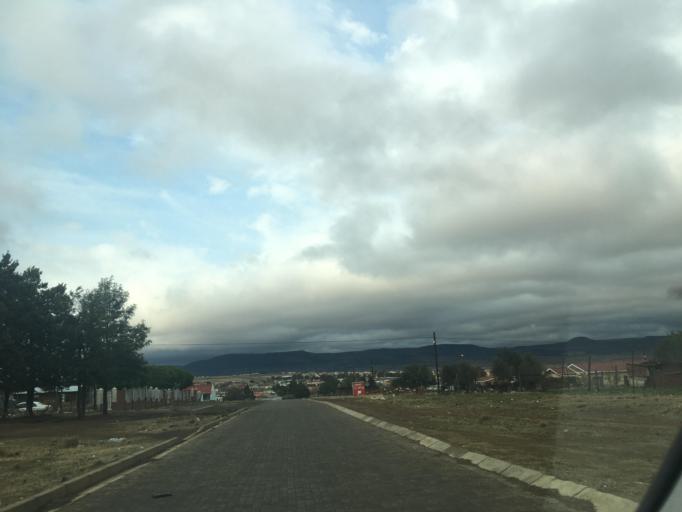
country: ZA
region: Eastern Cape
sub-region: Chris Hani District Municipality
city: Cala
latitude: -31.5270
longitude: 27.6993
